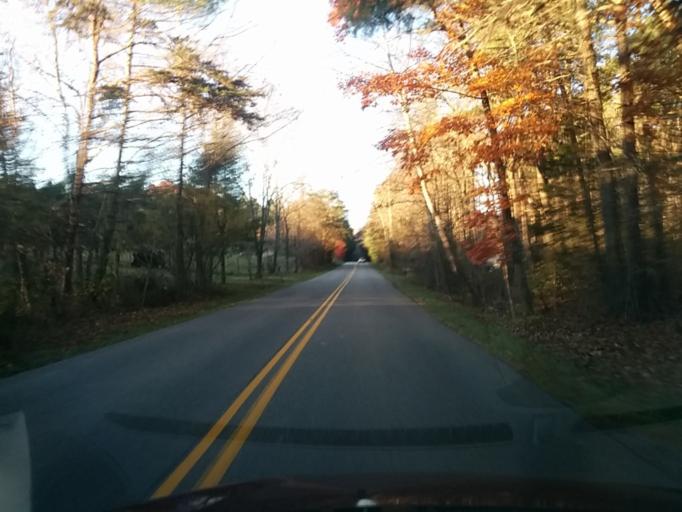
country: US
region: Virginia
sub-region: City of Lexington
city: Lexington
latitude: 37.9304
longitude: -79.5788
